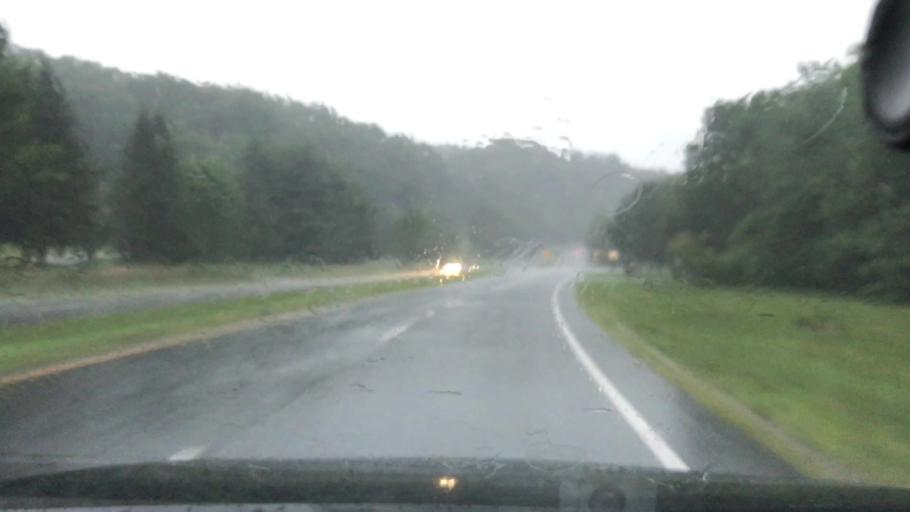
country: US
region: Virginia
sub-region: Giles County
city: Pearisburg
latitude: 37.3492
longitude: -80.7629
